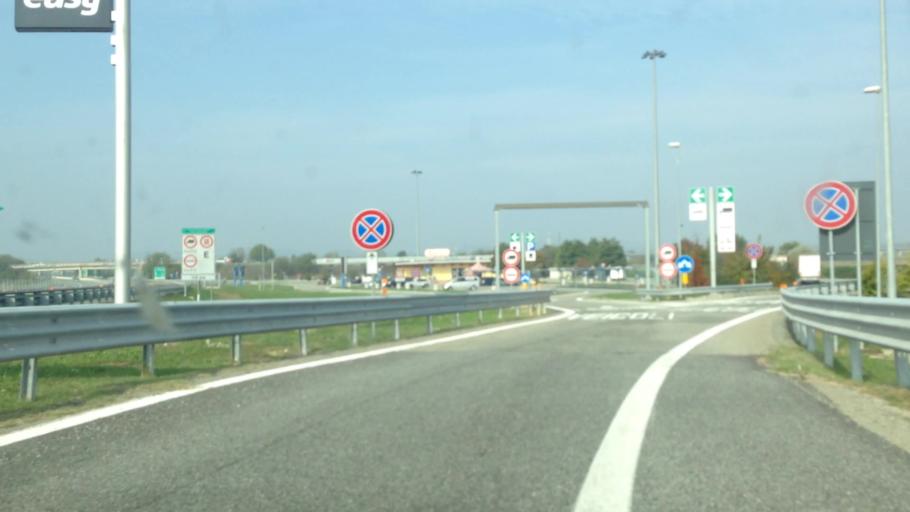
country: IT
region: Piedmont
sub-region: Provincia di Vercelli
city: Santhia
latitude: 45.3667
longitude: 8.1458
